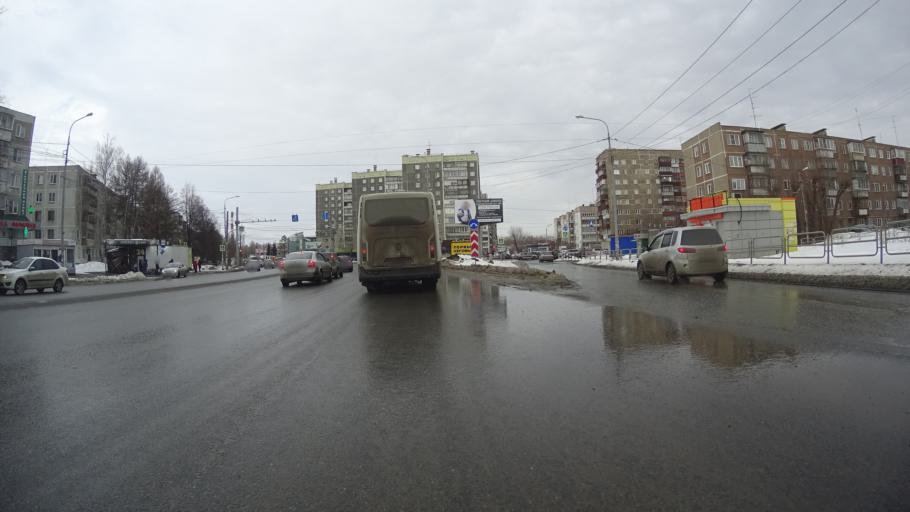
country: RU
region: Chelyabinsk
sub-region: Gorod Chelyabinsk
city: Chelyabinsk
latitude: 55.1977
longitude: 61.3327
